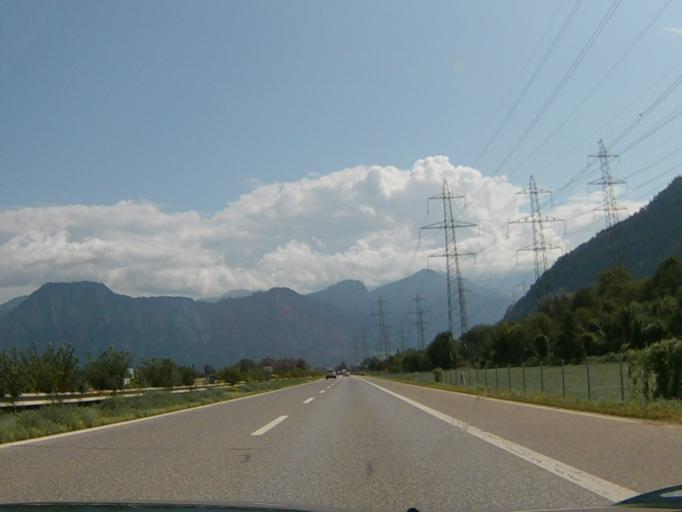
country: CH
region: Grisons
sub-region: Landquart District
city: Maienfeld
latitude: 46.9952
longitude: 9.5270
